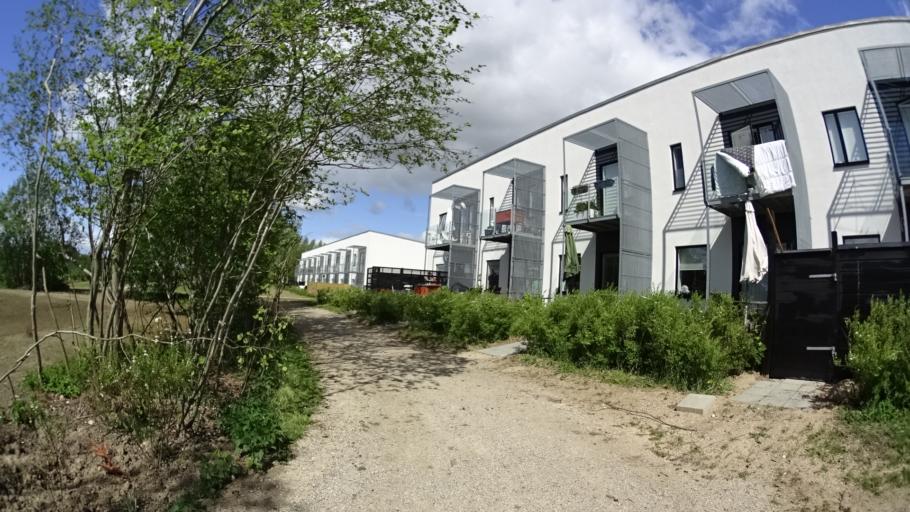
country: DK
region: Central Jutland
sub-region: Arhus Kommune
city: Stavtrup
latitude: 56.1266
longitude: 10.1029
